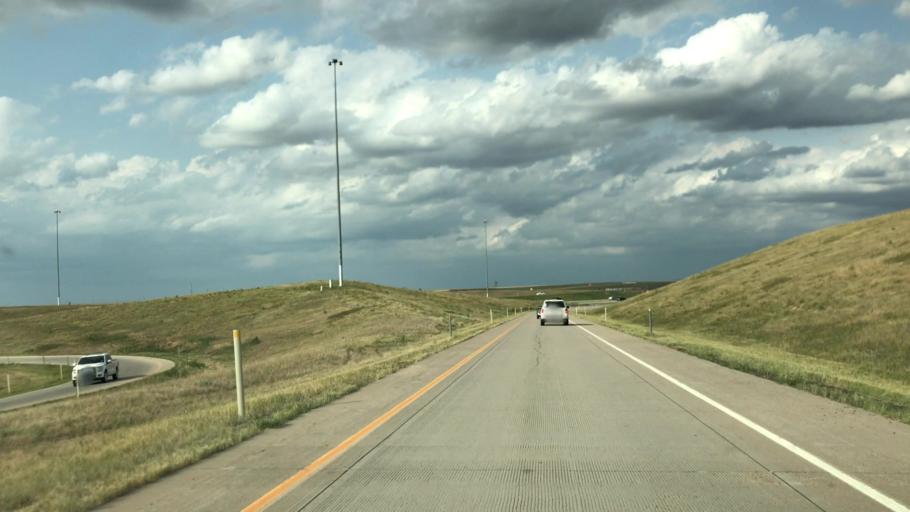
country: US
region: Colorado
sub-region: Adams County
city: Aurora
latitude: 39.8317
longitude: -104.7445
